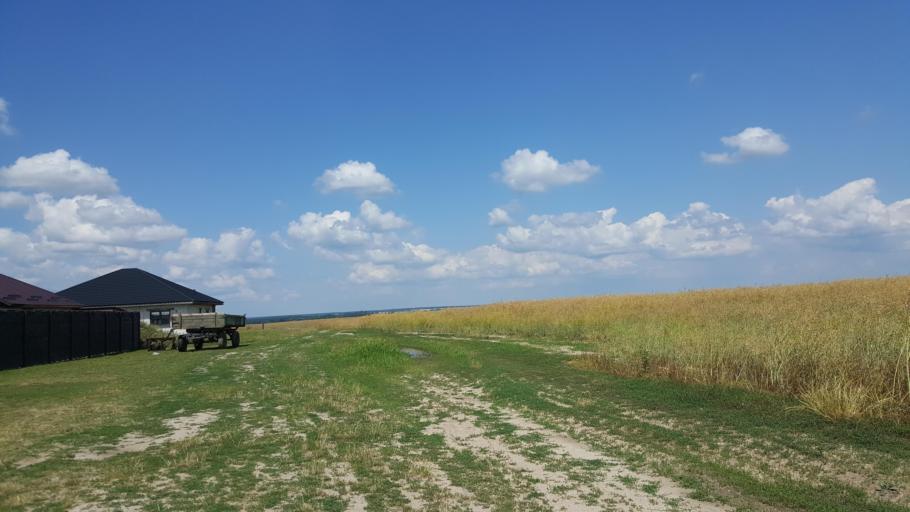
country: BY
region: Brest
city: Kamyanyets
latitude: 52.4045
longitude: 23.8486
